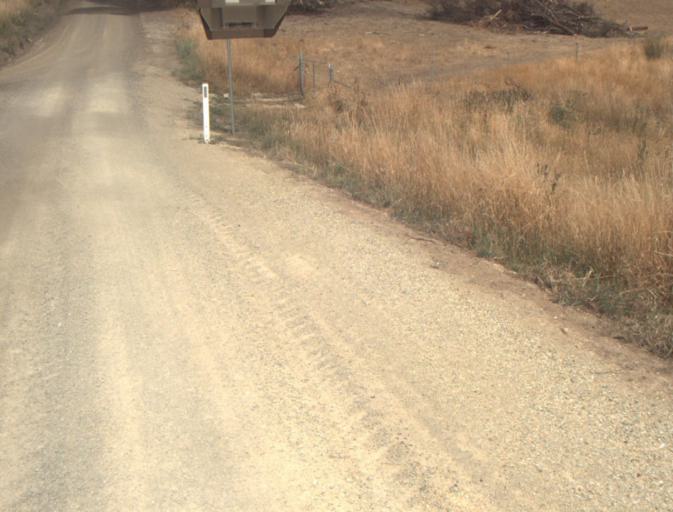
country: AU
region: Tasmania
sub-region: Launceston
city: Mayfield
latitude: -41.2121
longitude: 147.1428
